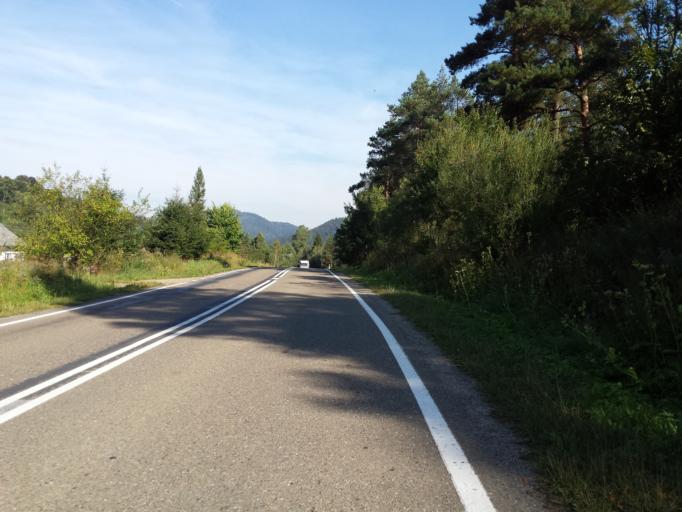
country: PL
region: Subcarpathian Voivodeship
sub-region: Powiat leski
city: Baligrod
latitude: 49.2713
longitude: 22.2890
